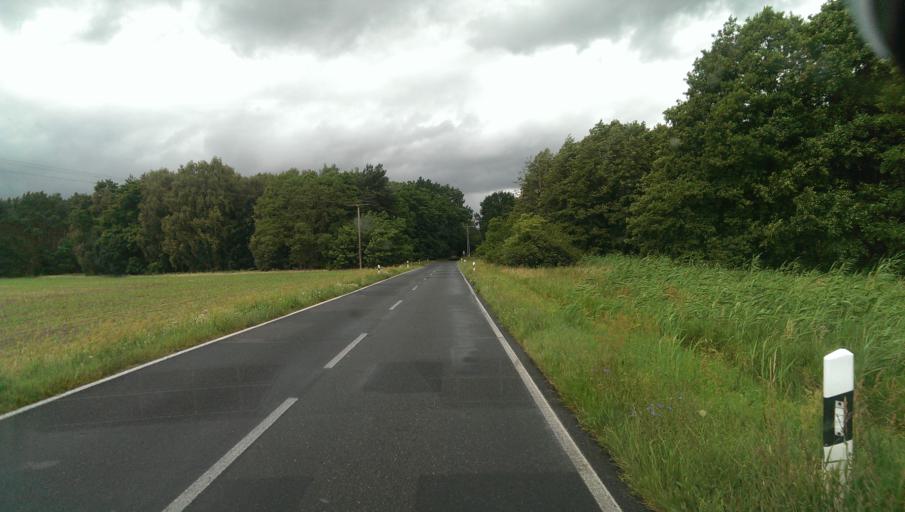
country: DE
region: Brandenburg
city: Brandenburg an der Havel
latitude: 52.3637
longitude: 12.6277
